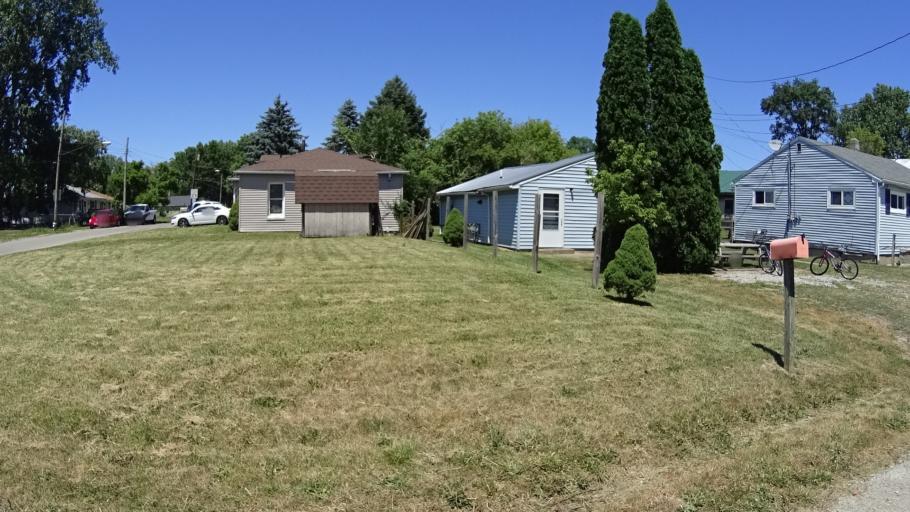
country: US
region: Ohio
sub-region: Erie County
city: Sandusky
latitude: 41.4287
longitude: -82.7003
